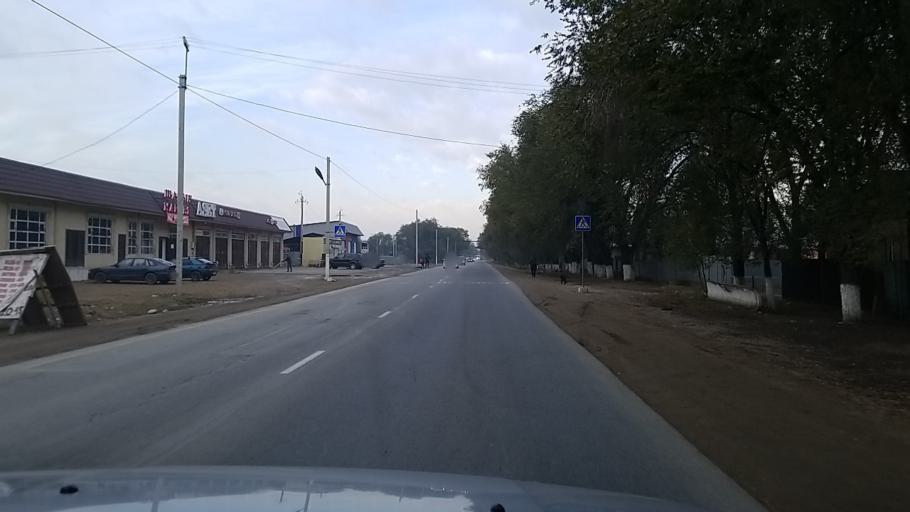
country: KZ
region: Almaty Oblysy
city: Burunday
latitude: 43.3552
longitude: 76.8069
